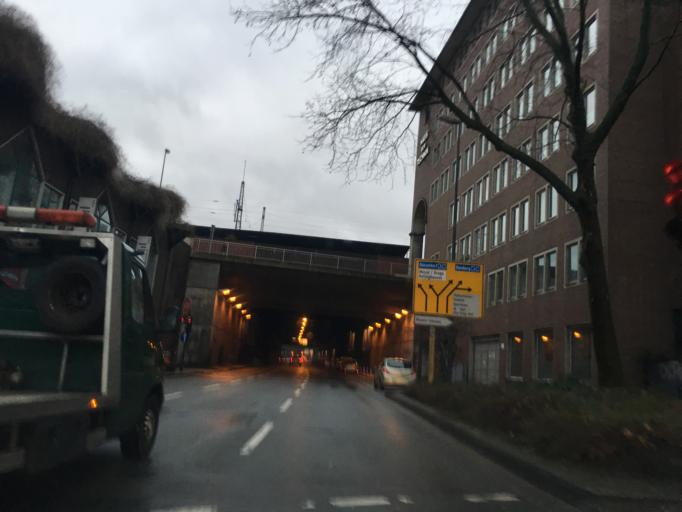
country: DE
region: North Rhine-Westphalia
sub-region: Regierungsbezirk Dusseldorf
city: Essen
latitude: 51.4532
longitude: 7.0159
